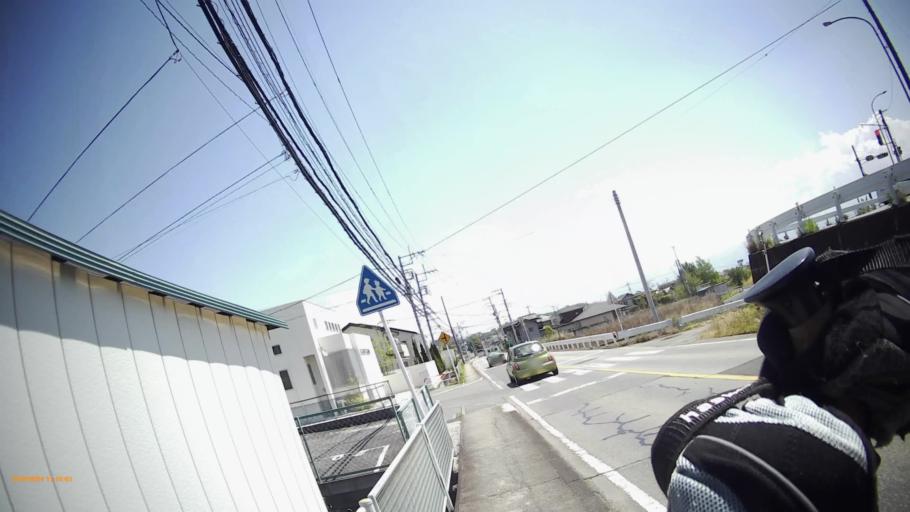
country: JP
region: Yamanashi
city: Nirasaki
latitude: 35.6914
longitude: 138.4756
